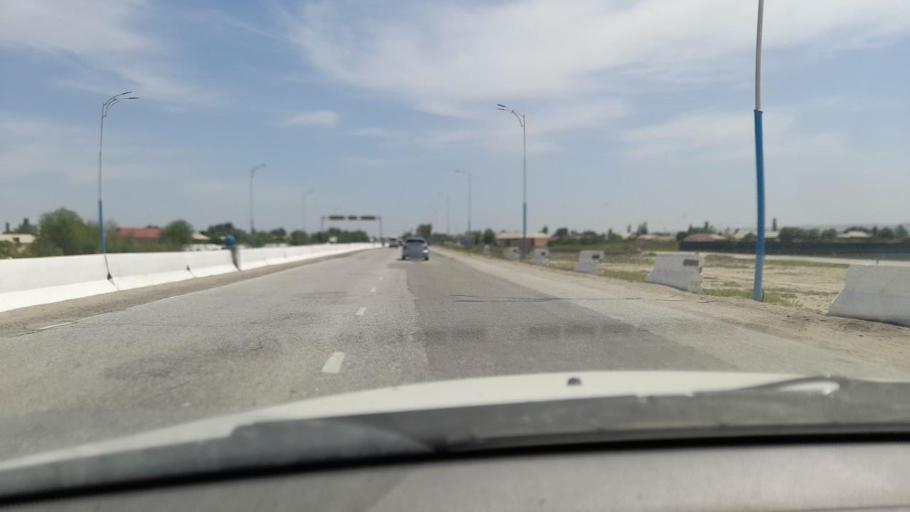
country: UZ
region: Navoiy
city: Navoiy
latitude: 40.1170
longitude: 65.4931
